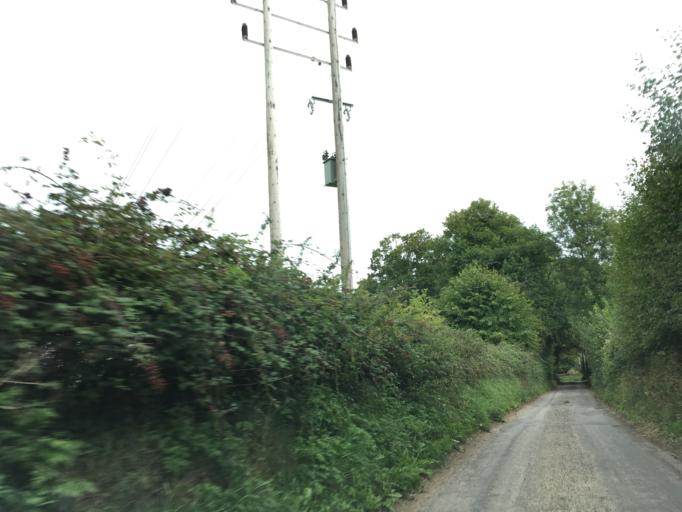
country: GB
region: England
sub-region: South Gloucestershire
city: Charfield
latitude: 51.6238
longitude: -2.4118
